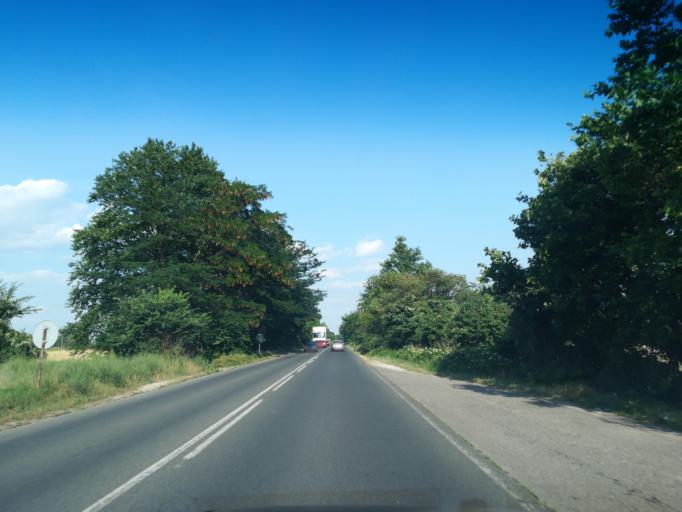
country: BG
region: Plovdiv
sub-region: Obshtina Plovdiv
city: Plovdiv
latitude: 42.1481
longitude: 24.8349
